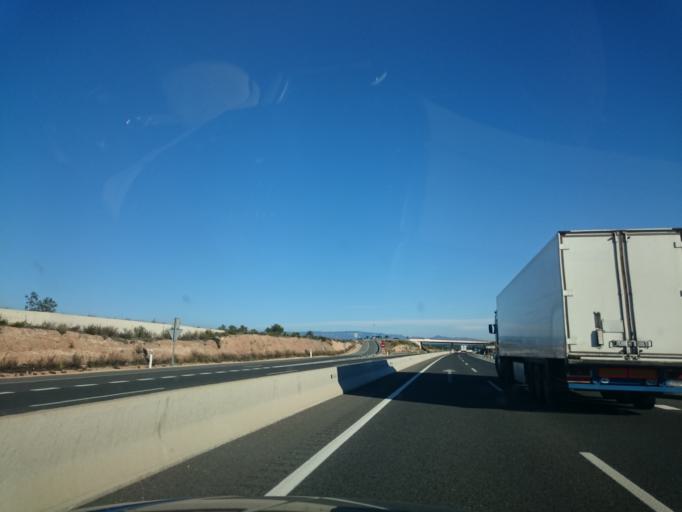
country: ES
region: Catalonia
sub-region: Provincia de Tarragona
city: Colldejou
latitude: 41.0213
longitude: 0.9282
